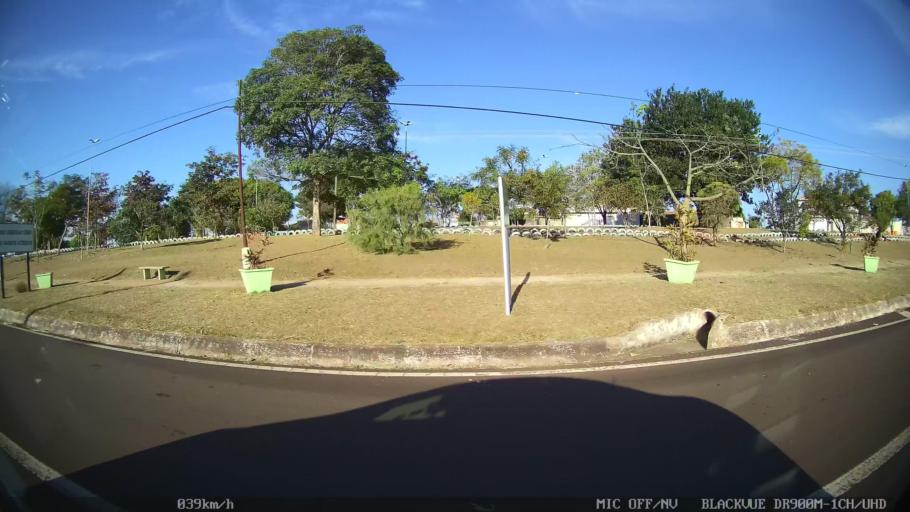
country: BR
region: Sao Paulo
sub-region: Franca
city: Franca
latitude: -20.5083
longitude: -47.3725
